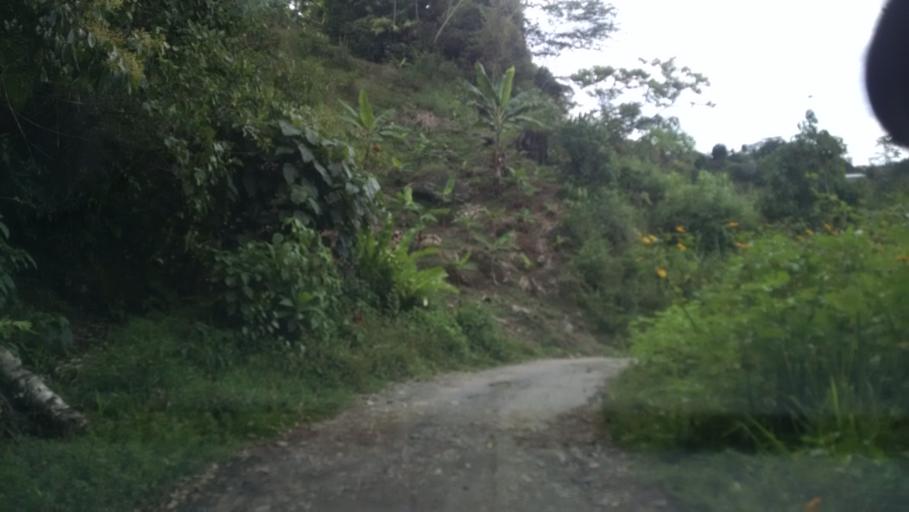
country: CO
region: Antioquia
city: Cocorna
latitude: 6.0226
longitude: -75.1666
